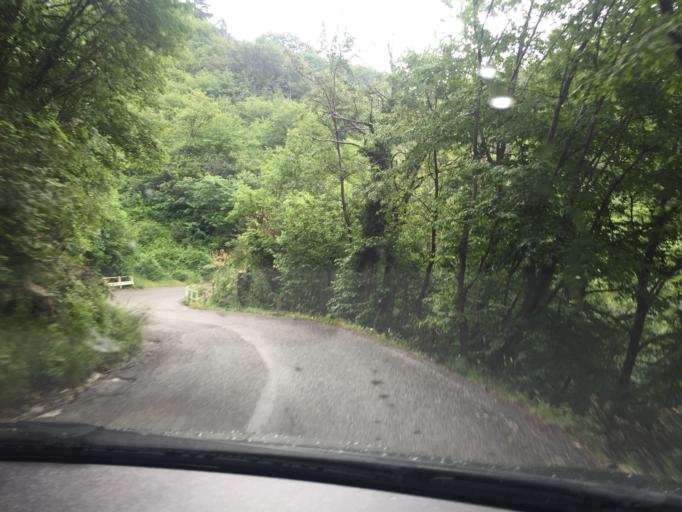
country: IT
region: Lombardy
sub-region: Provincia di Lecco
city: Esino Lario
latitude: 45.9959
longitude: 9.3421
